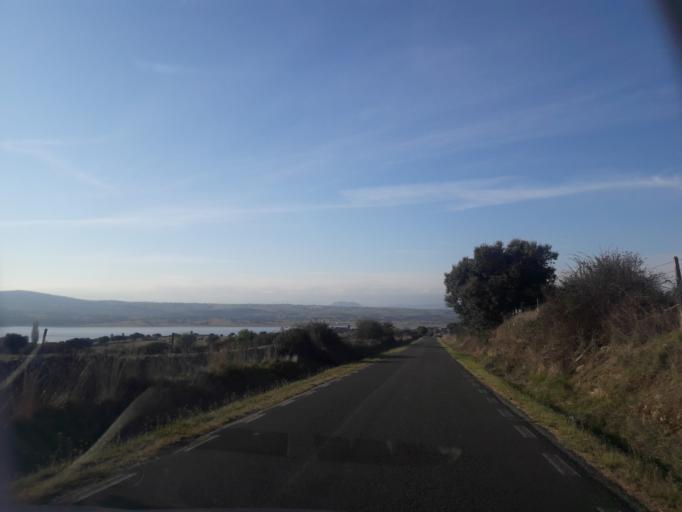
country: ES
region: Castille and Leon
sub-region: Provincia de Salamanca
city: Salvatierra de Tormes
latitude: 40.5997
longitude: -5.5995
